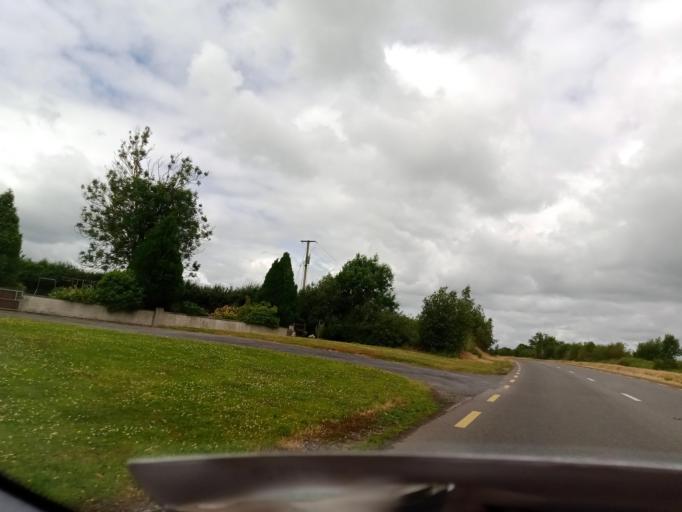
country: IE
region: Leinster
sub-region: Kilkenny
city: Thomastown
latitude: 52.4854
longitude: -7.2259
